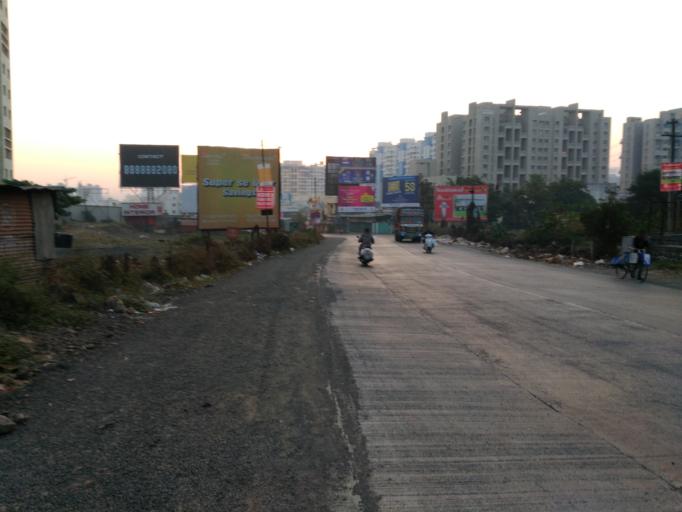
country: IN
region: Maharashtra
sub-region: Pune Division
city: Pune
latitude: 18.4500
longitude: 73.9020
